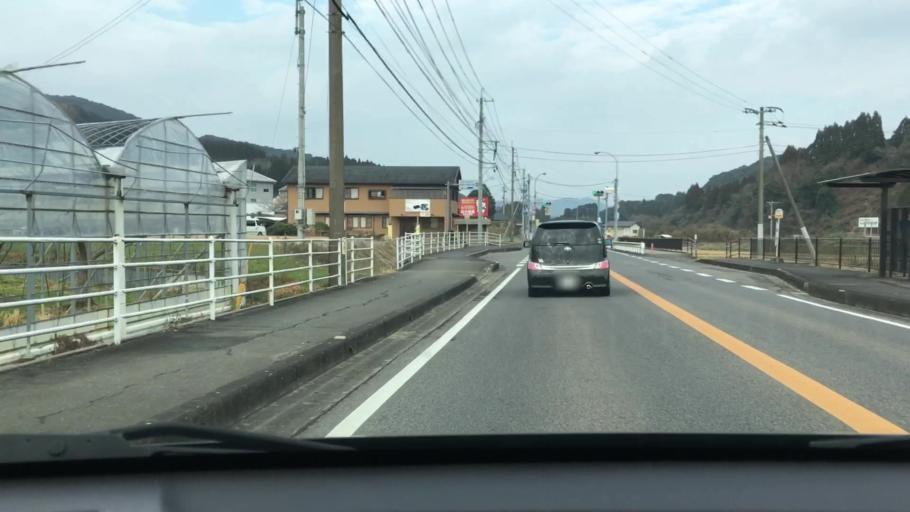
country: JP
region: Saga Prefecture
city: Imaricho-ko
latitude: 33.3162
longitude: 129.9289
